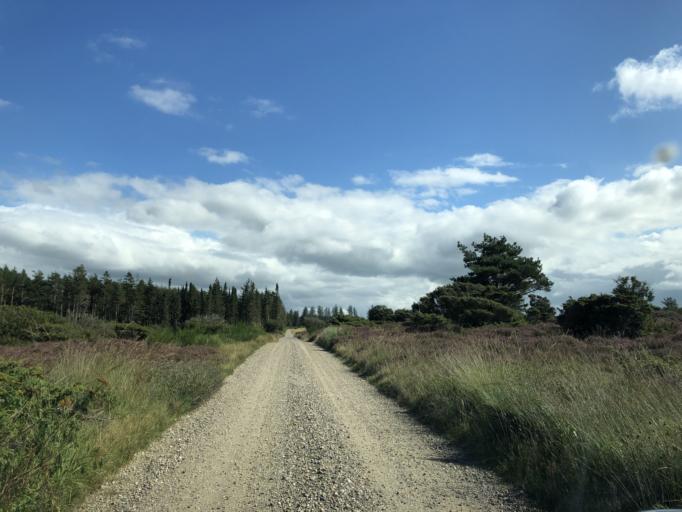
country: DK
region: Central Jutland
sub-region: Holstebro Kommune
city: Ulfborg
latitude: 56.2487
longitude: 8.4799
